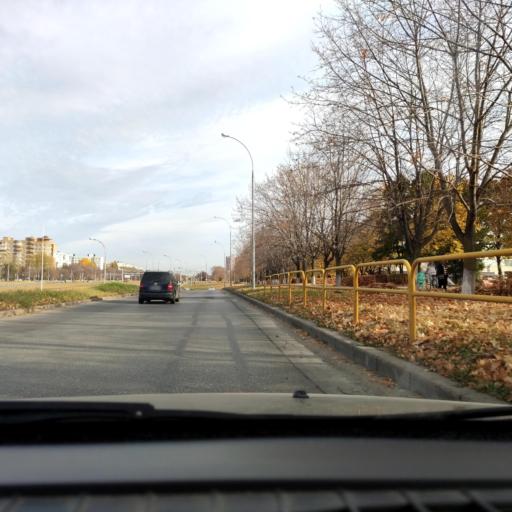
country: RU
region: Samara
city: Tol'yatti
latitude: 53.5198
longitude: 49.2745
